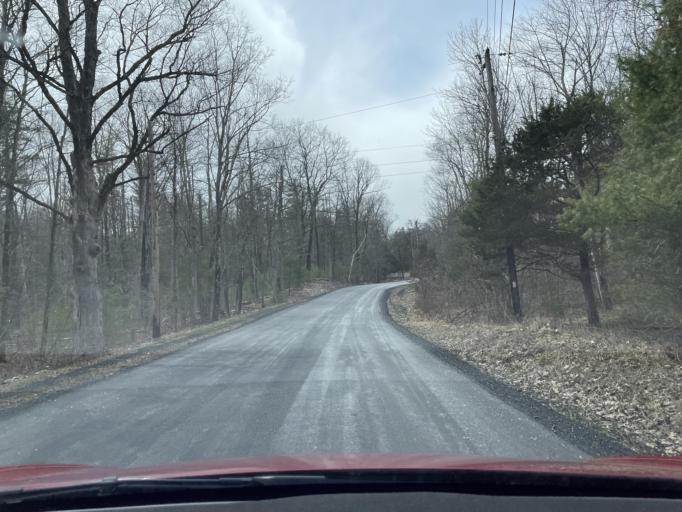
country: US
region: New York
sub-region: Ulster County
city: Manorville
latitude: 42.0850
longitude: -74.0338
